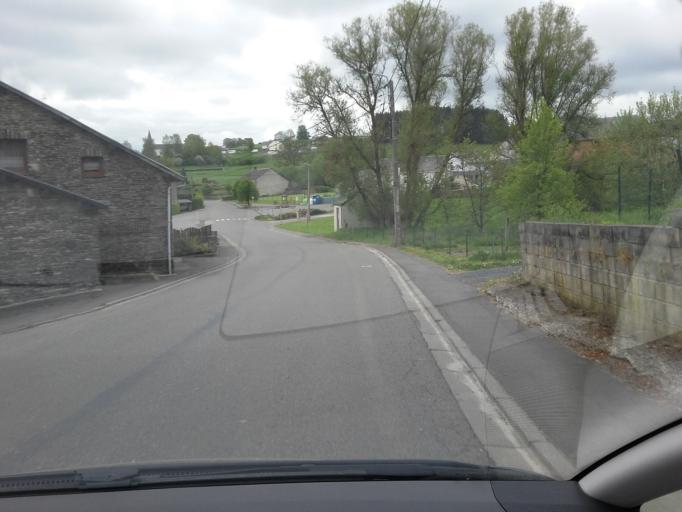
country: BE
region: Wallonia
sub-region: Province du Luxembourg
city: Bertrix
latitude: 49.8217
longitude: 5.3241
